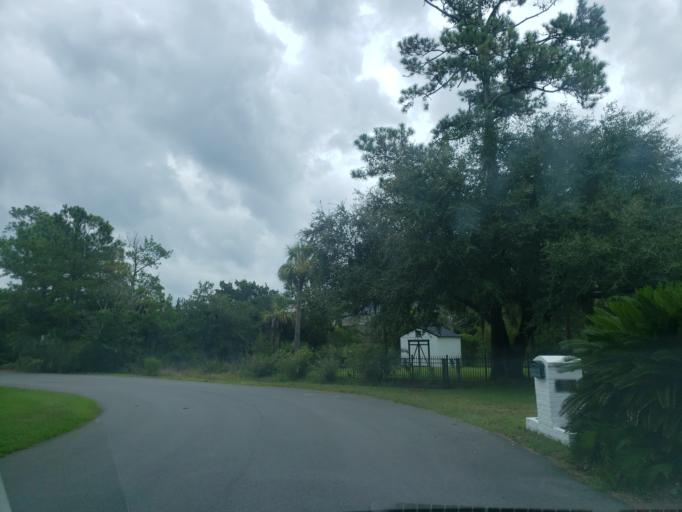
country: US
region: Georgia
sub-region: Chatham County
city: Wilmington Island
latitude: 32.0103
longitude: -80.9563
